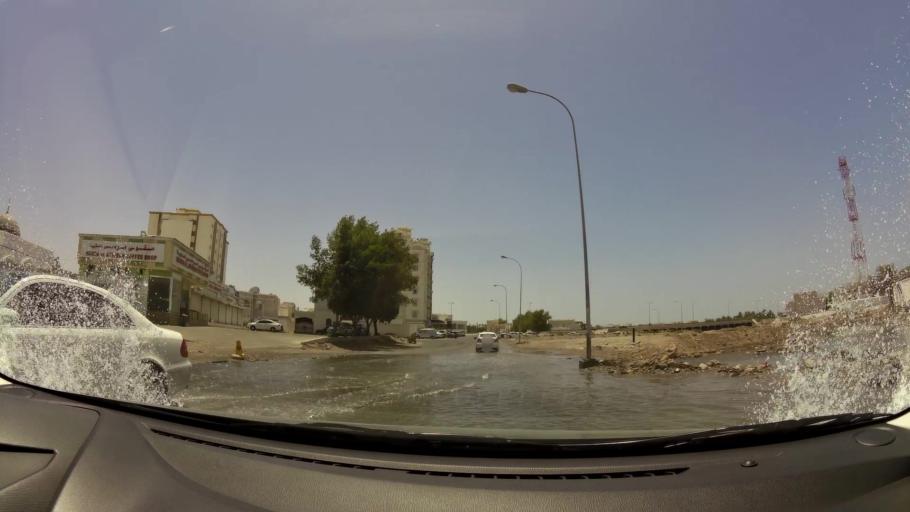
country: OM
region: Muhafazat Masqat
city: Bawshar
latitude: 23.5942
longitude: 58.3866
